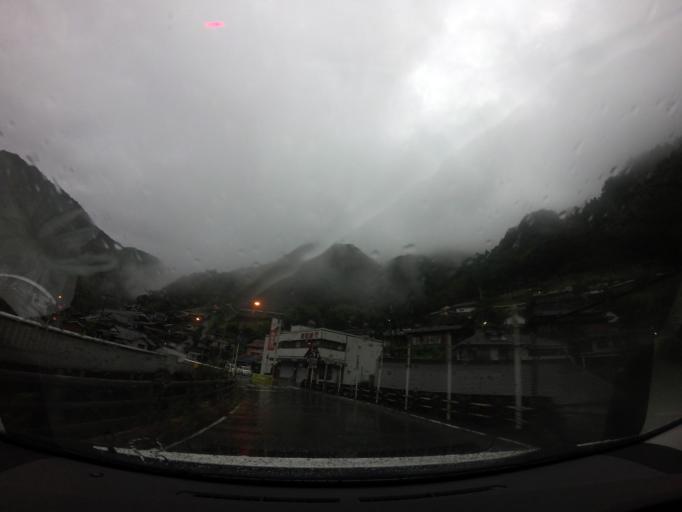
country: JP
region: Wakayama
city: Shingu
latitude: 33.9484
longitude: 135.8043
